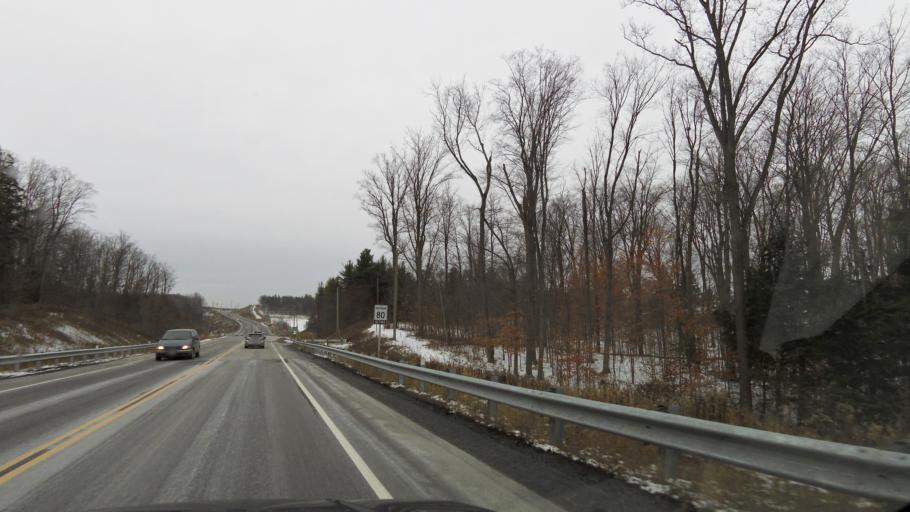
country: CA
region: Ontario
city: Newmarket
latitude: 44.0700
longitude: -79.5115
